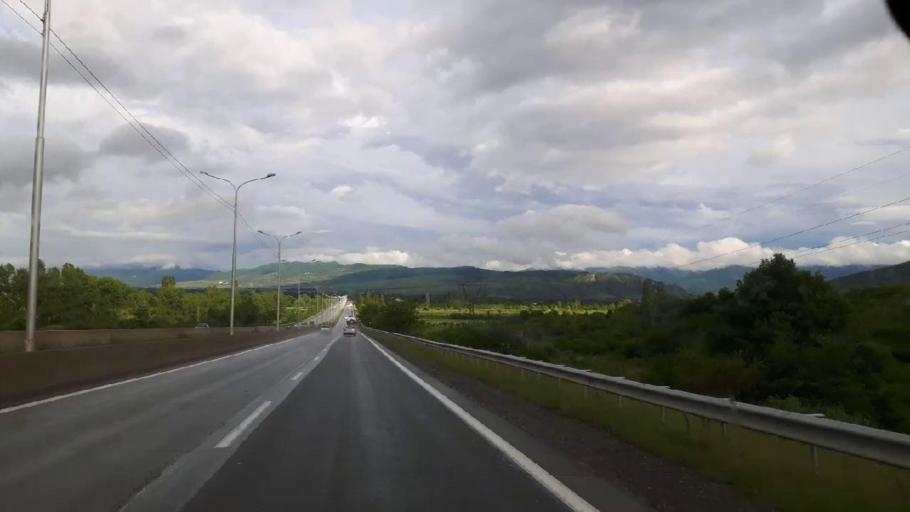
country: GE
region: Shida Kartli
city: Kaspi
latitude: 41.9263
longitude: 44.5359
